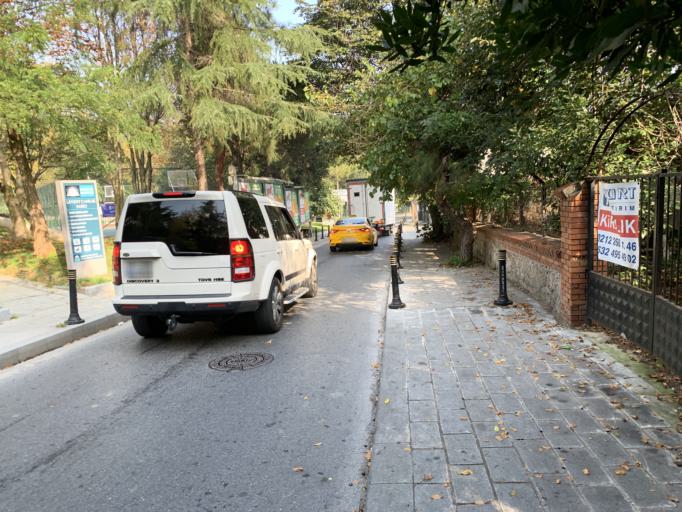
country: TR
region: Istanbul
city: Sisli
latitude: 41.0847
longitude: 29.0145
